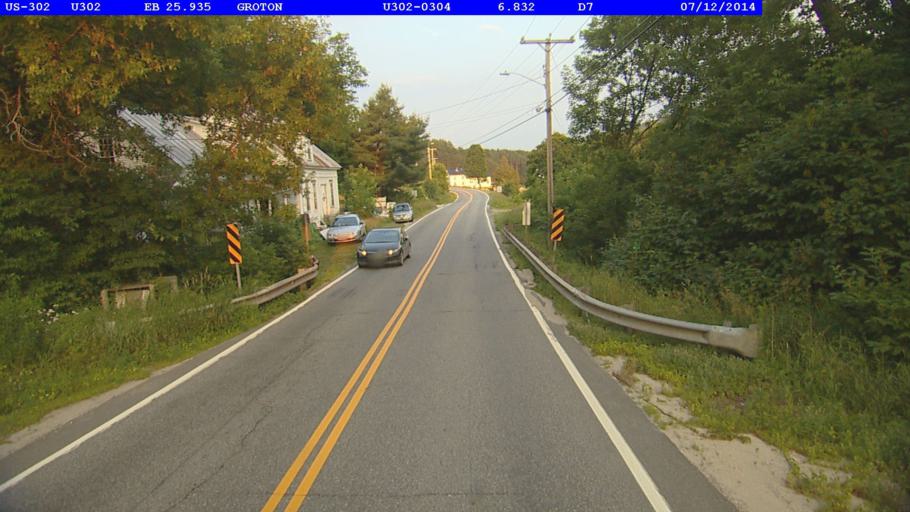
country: US
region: New Hampshire
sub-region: Grafton County
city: Woodsville
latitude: 44.2087
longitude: -72.1900
